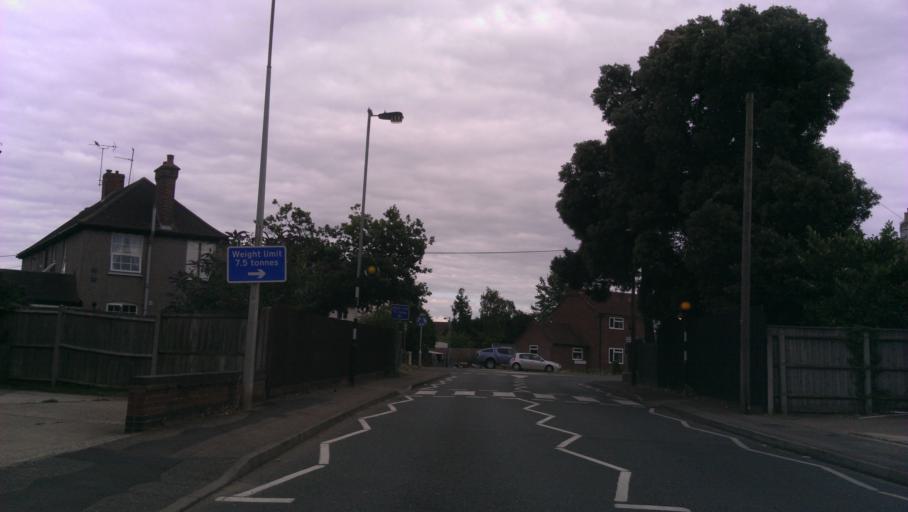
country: GB
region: England
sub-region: Essex
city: Eight Ash Green
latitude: 51.8798
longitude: 0.8339
